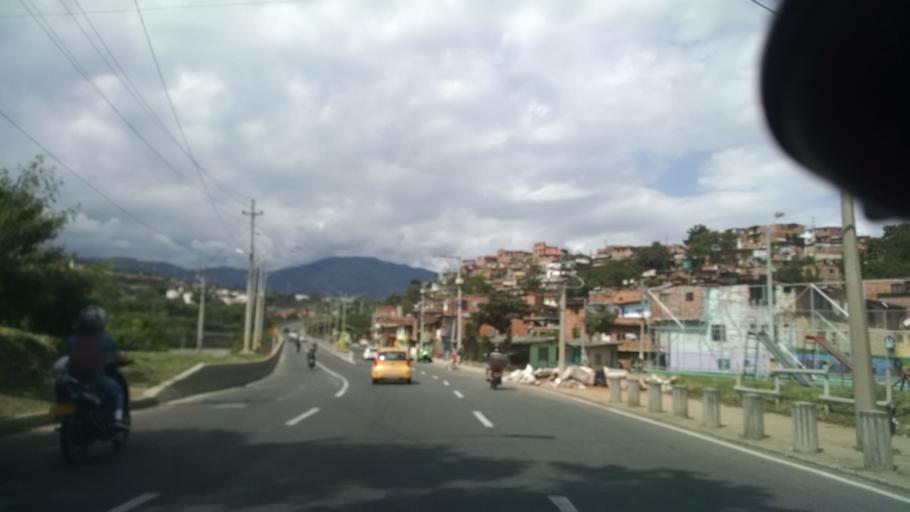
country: CO
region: Antioquia
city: Medellin
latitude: 6.2806
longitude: -75.5681
